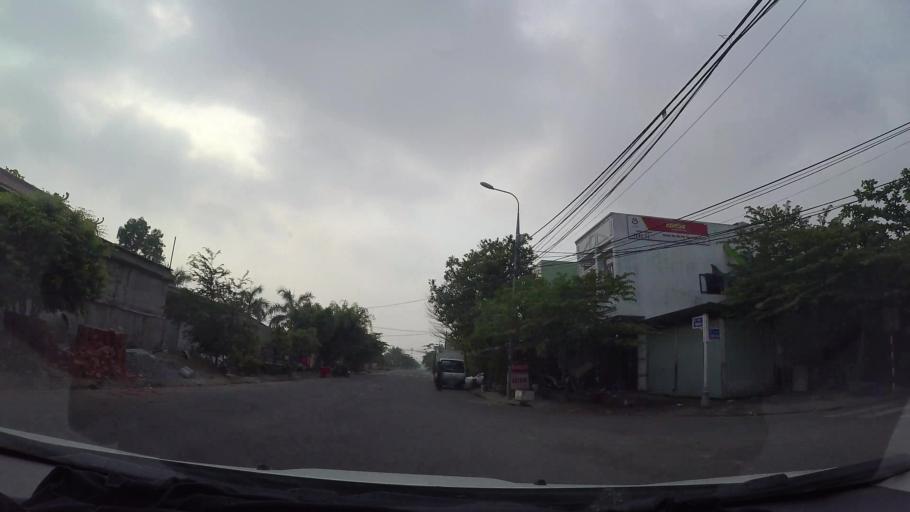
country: VN
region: Da Nang
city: Cam Le
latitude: 16.0054
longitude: 108.2183
